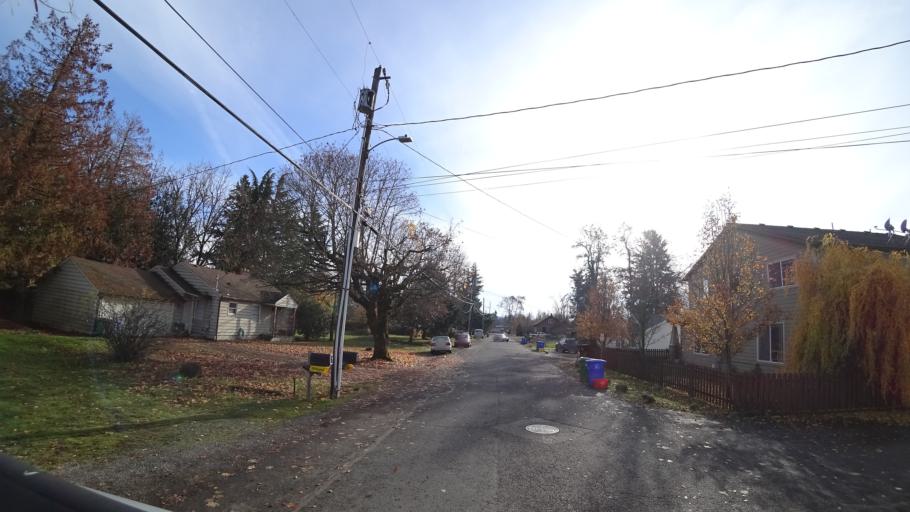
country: US
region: Oregon
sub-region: Multnomah County
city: Lents
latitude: 45.5212
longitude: -122.5159
